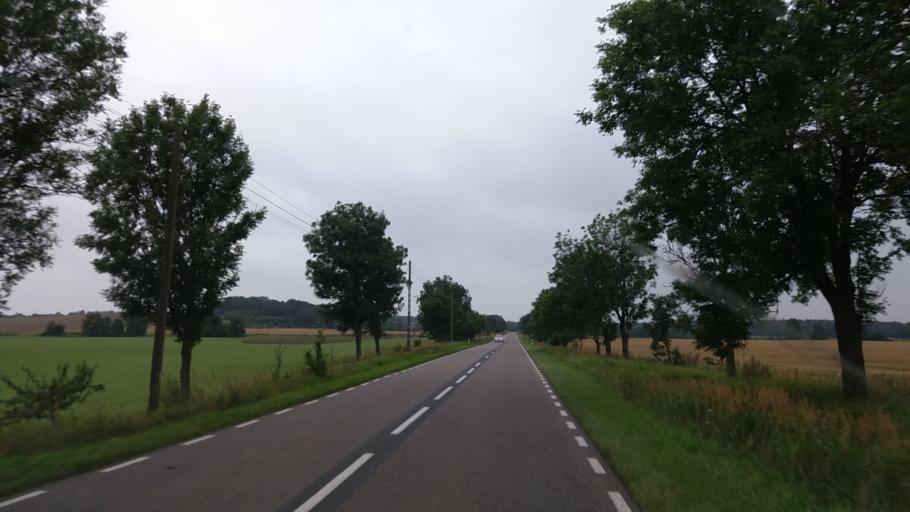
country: PL
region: West Pomeranian Voivodeship
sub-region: Powiat choszczenski
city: Pelczyce
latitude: 53.0199
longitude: 15.2801
